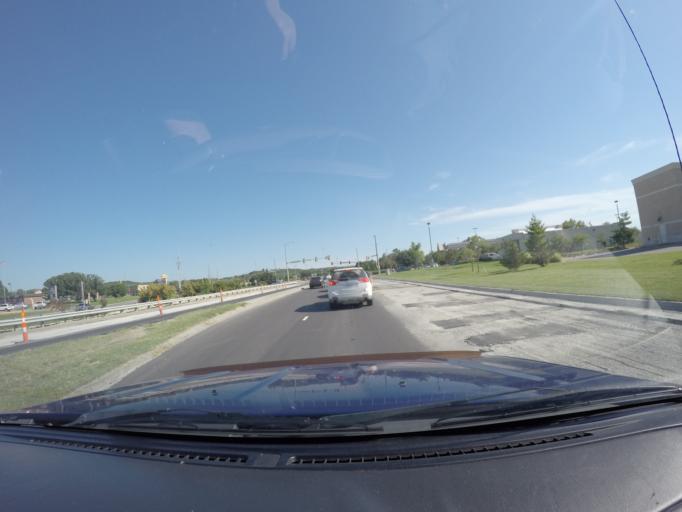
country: US
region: Kansas
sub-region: Riley County
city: Manhattan
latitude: 39.1823
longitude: -96.5585
